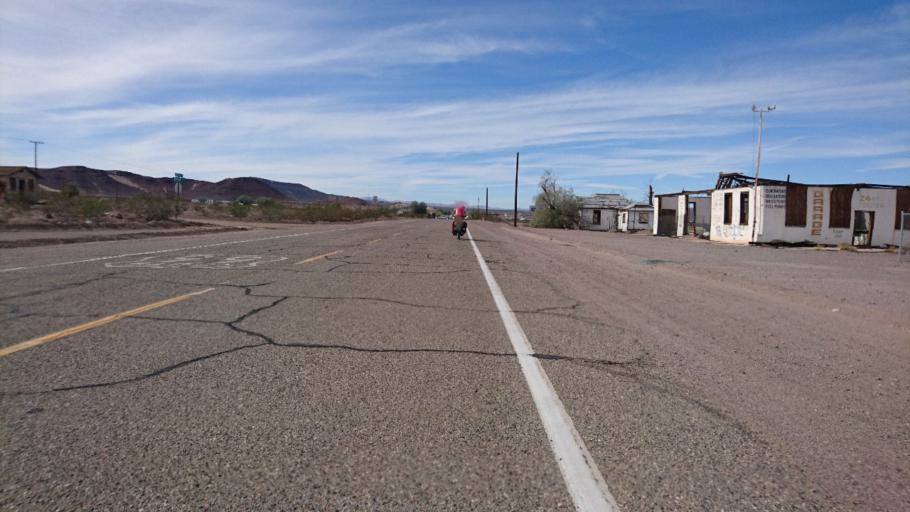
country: US
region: California
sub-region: San Bernardino County
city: Twentynine Palms
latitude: 34.7240
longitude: -116.1584
